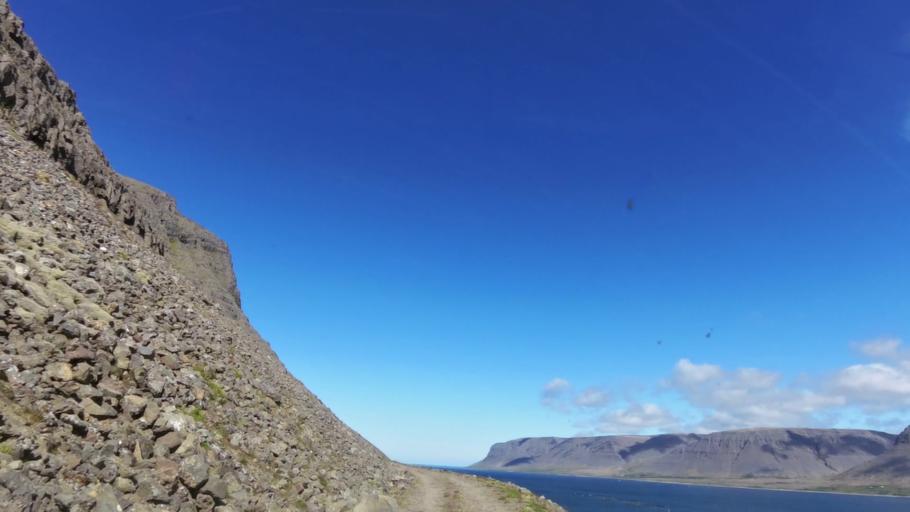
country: IS
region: West
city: Olafsvik
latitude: 65.6276
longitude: -23.9033
